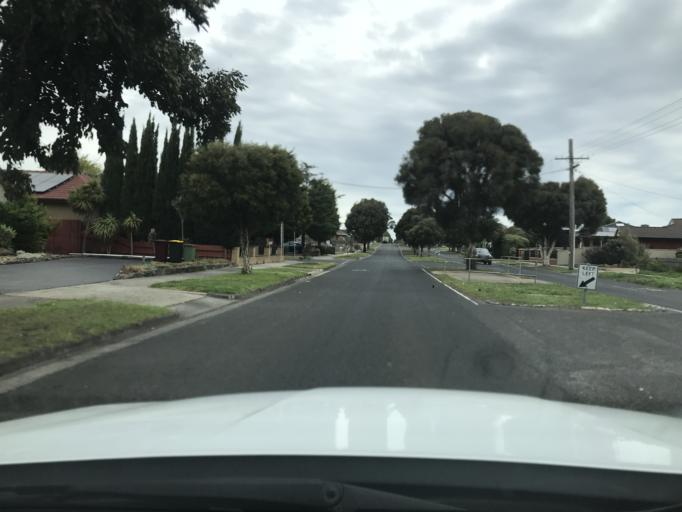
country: AU
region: Victoria
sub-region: Hume
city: Craigieburn
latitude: -37.5935
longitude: 144.9374
